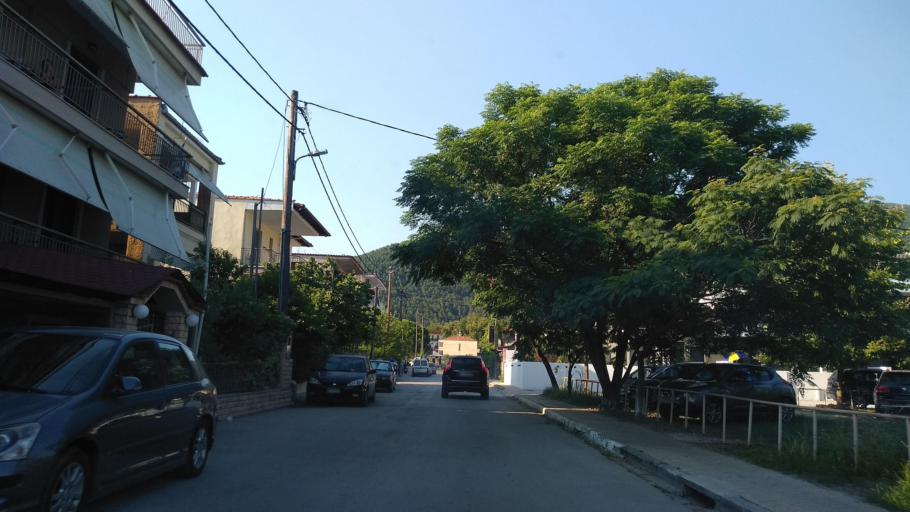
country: GR
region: Central Macedonia
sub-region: Nomos Thessalonikis
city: Stavros
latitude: 40.6664
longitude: 23.6920
